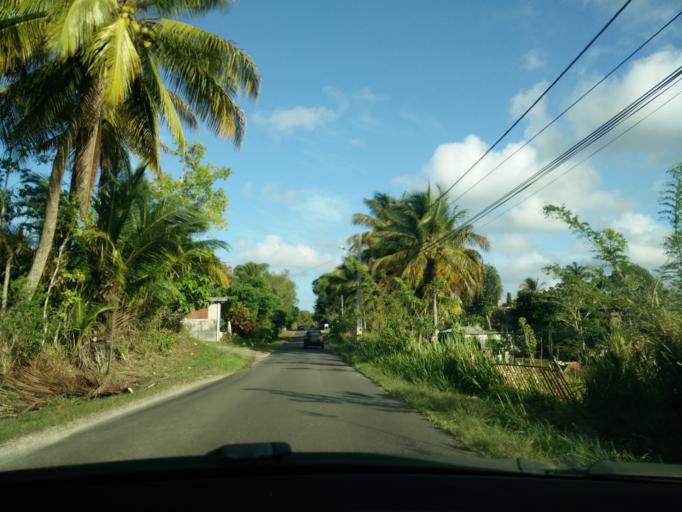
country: GP
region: Guadeloupe
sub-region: Guadeloupe
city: Sainte-Anne
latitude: 16.2767
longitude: -61.3977
